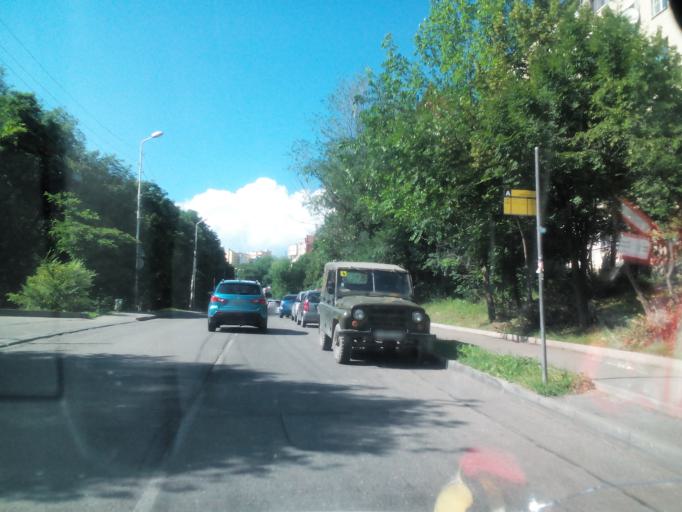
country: RU
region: Stavropol'skiy
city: Pyatigorsk
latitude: 44.0455
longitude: 43.0688
